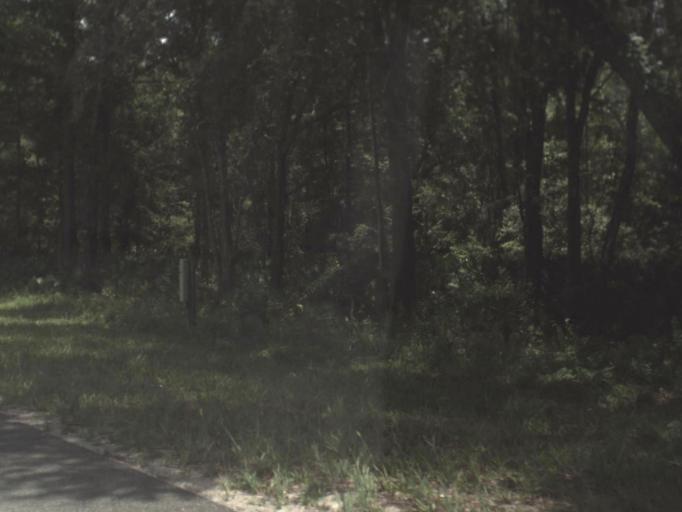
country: US
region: Florida
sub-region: Taylor County
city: Perry
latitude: 30.1426
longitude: -83.7853
